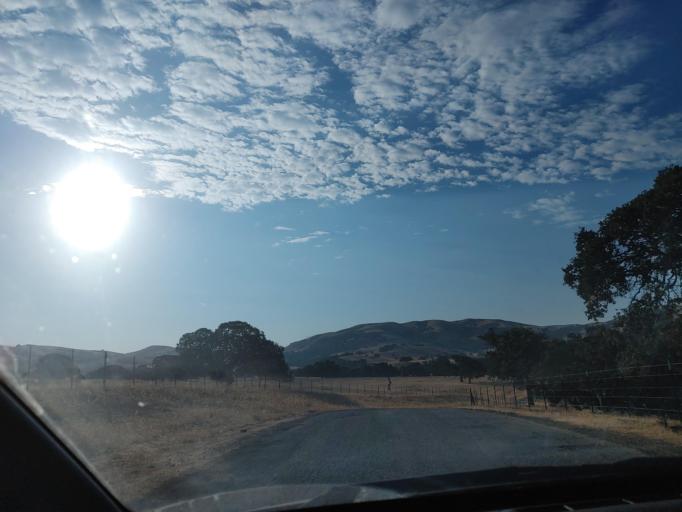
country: US
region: California
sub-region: San Benito County
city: Ridgemark
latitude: 36.7754
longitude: -121.2379
